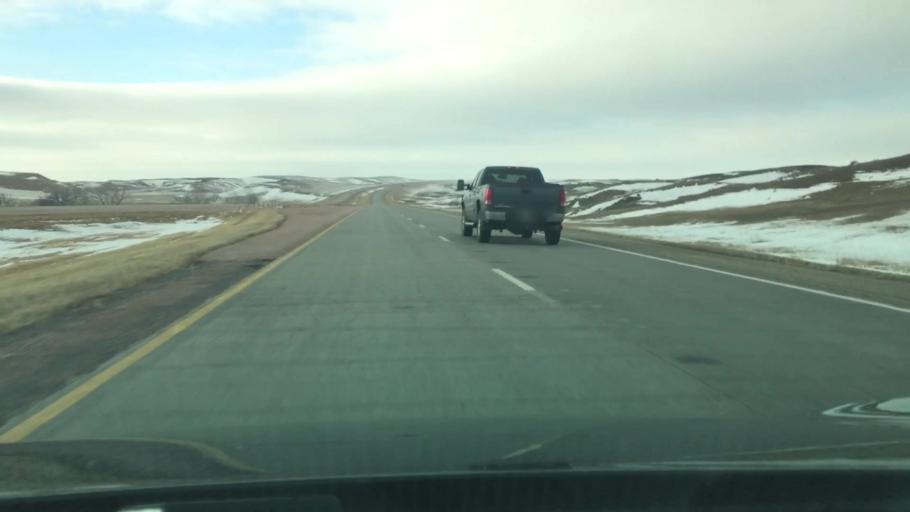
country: US
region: South Dakota
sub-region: Brule County
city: Chamberlain
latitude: 43.8210
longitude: -99.4394
